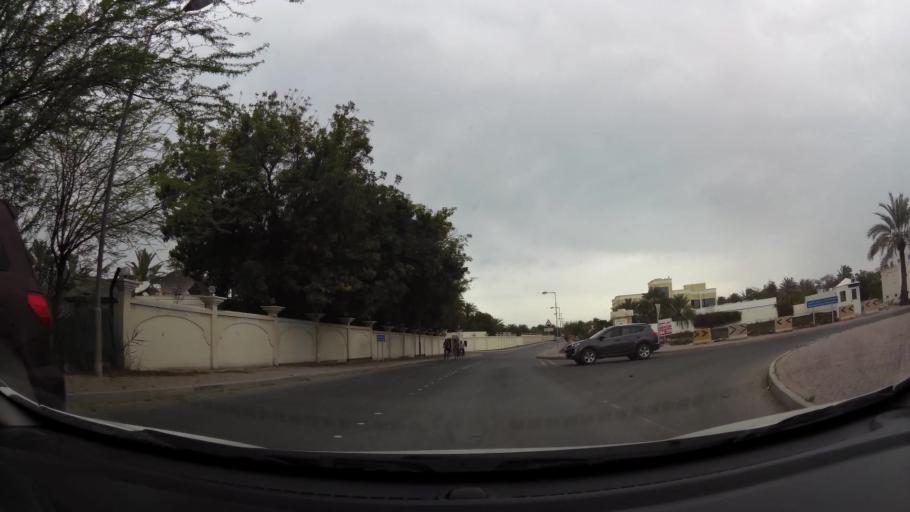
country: BH
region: Central Governorate
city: Madinat Hamad
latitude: 26.1485
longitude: 50.4554
